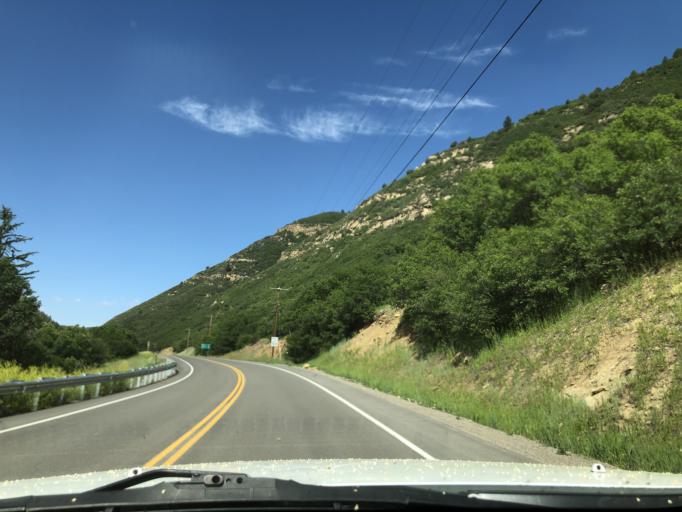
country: US
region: Colorado
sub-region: Delta County
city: Paonia
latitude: 38.9414
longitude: -107.3636
